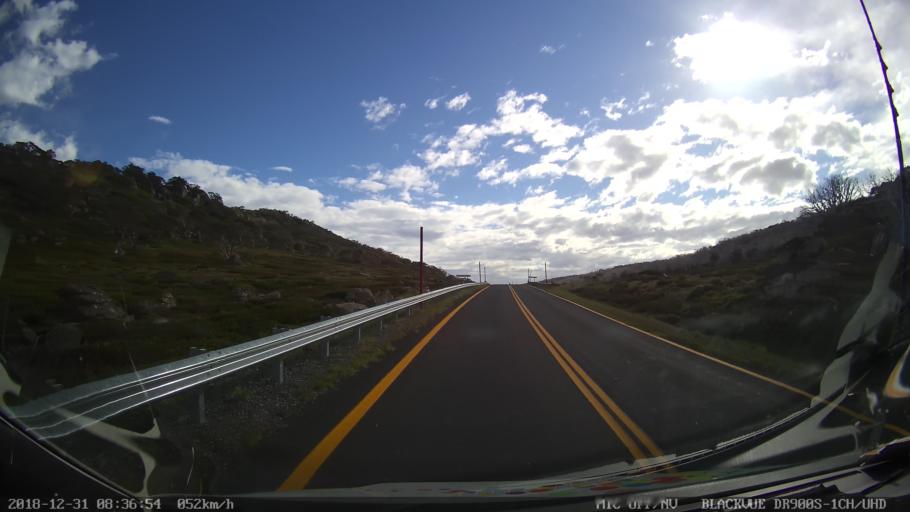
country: AU
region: New South Wales
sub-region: Snowy River
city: Jindabyne
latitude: -36.4217
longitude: 148.3804
